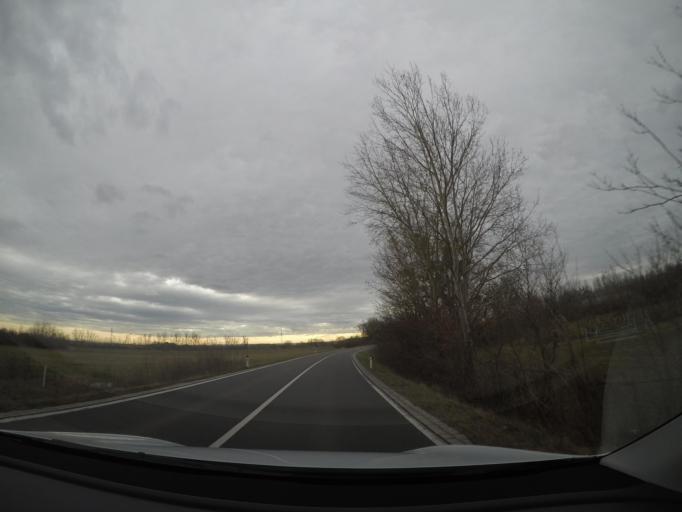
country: AT
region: Lower Austria
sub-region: Politischer Bezirk Modling
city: Biedermannsdorf
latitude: 48.0919
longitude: 16.3577
